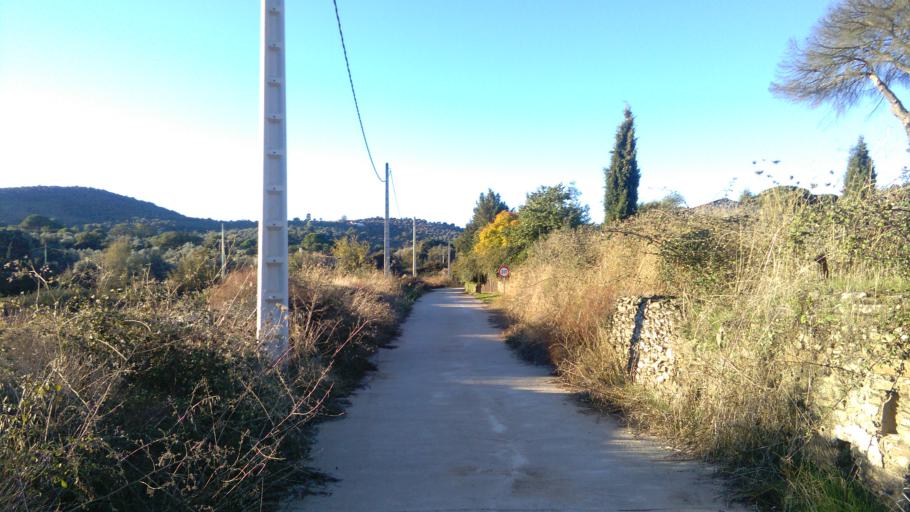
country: ES
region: Extremadura
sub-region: Provincia de Caceres
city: Herguijuela
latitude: 39.3950
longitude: -5.7846
